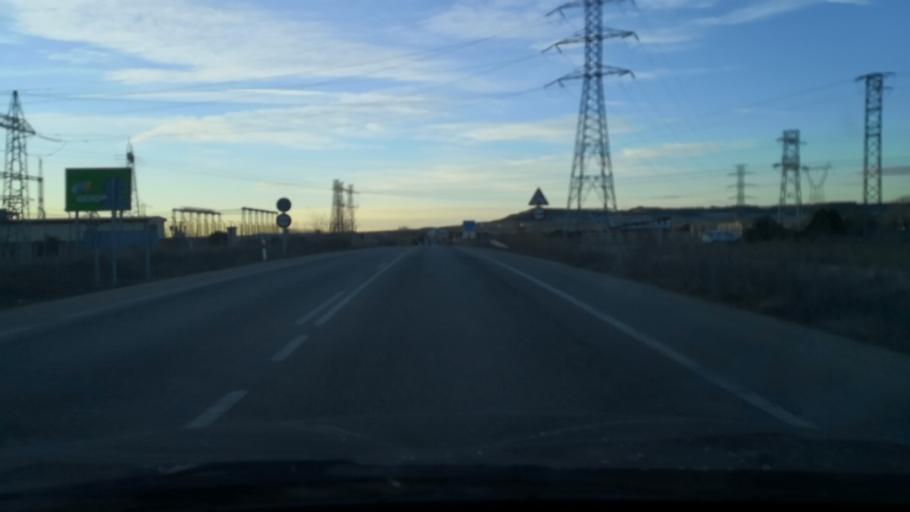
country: ES
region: Castille and Leon
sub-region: Provincia de Valladolid
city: Tordesillas
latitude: 41.5073
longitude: -5.0113
